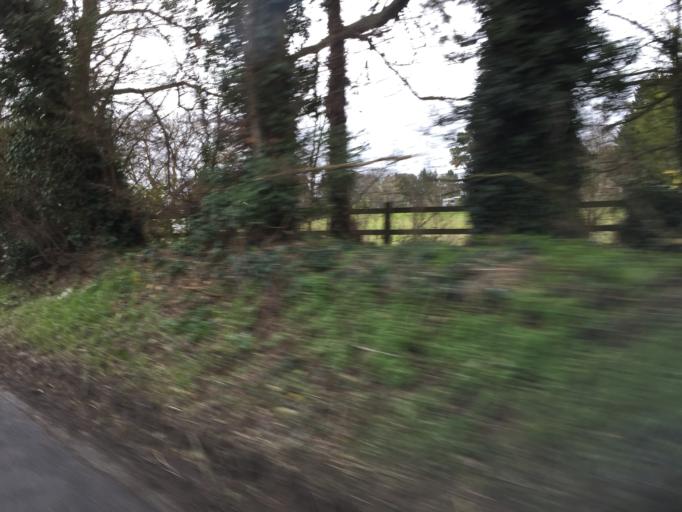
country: GB
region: England
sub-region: Oxfordshire
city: Blewbury
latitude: 51.5756
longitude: -1.2605
